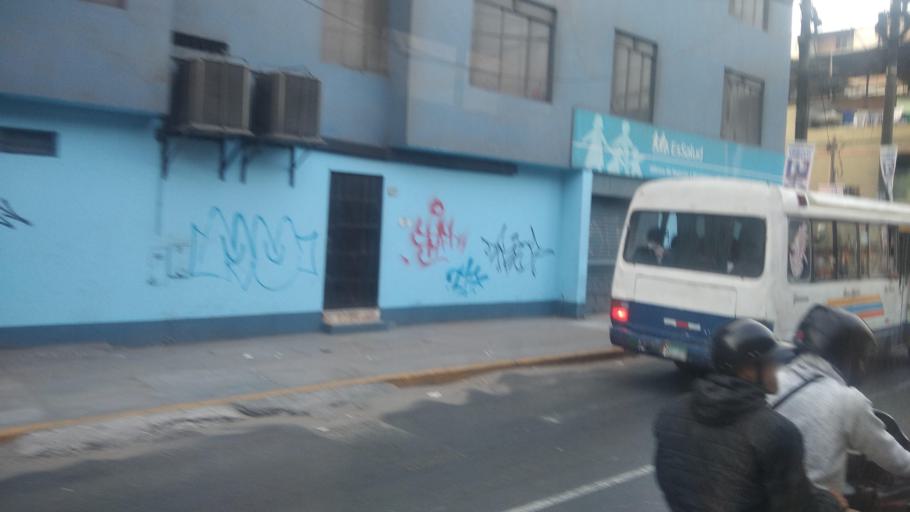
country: PE
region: Lima
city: Lima
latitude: -12.0230
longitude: -77.0008
